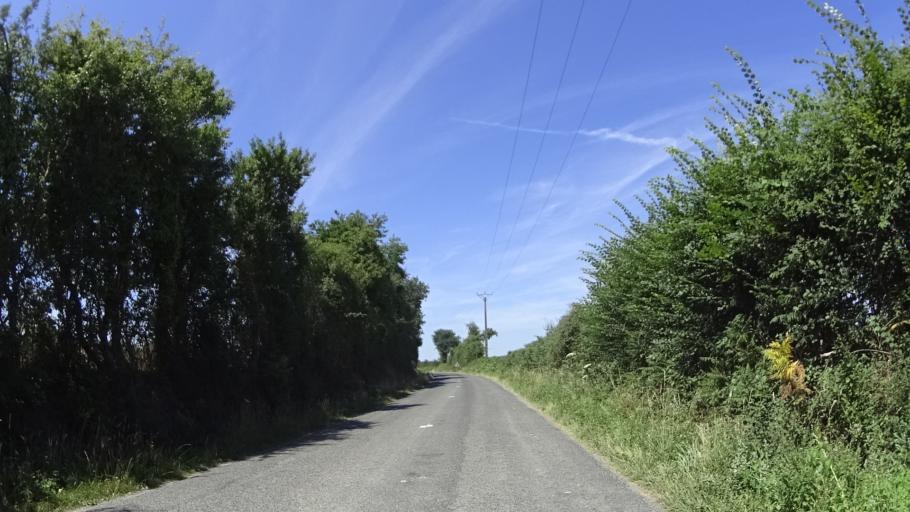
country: FR
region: Pays de la Loire
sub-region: Departement de Maine-et-Loire
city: Grez-Neuville
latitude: 47.6312
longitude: -0.7656
